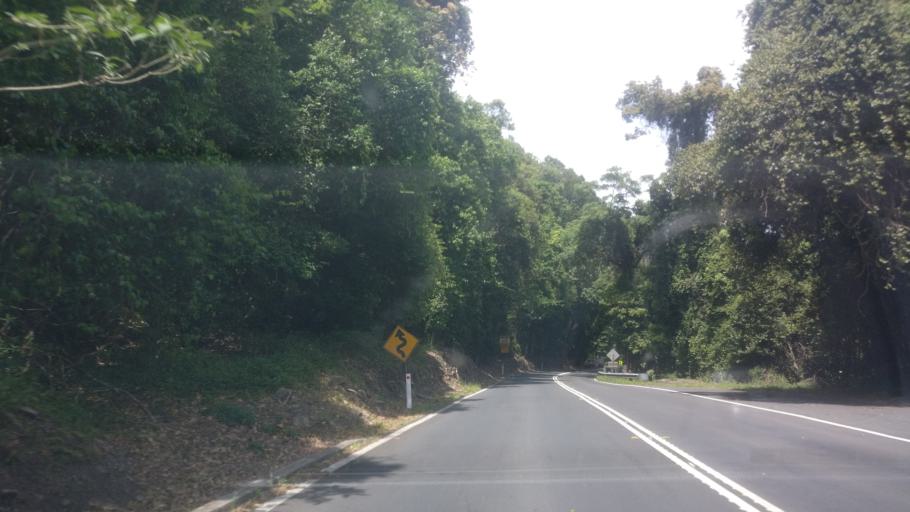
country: AU
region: New South Wales
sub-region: Shoalhaven Shire
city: Kangaroo Valley
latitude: -34.7921
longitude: 150.5662
